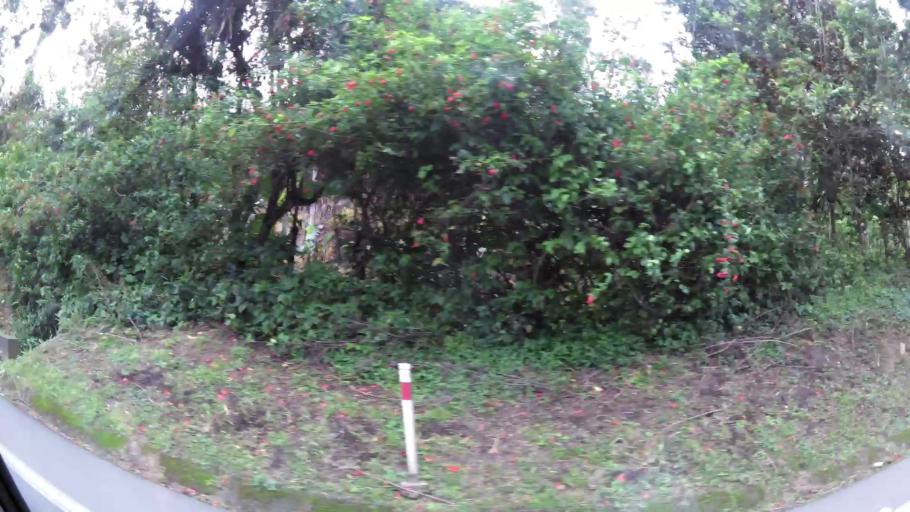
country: EC
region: Santo Domingo de los Tsachilas
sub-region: Canton Santo Domingo de los Colorados
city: Santo Domingo de los Colorados
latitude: -0.2821
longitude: -79.0710
